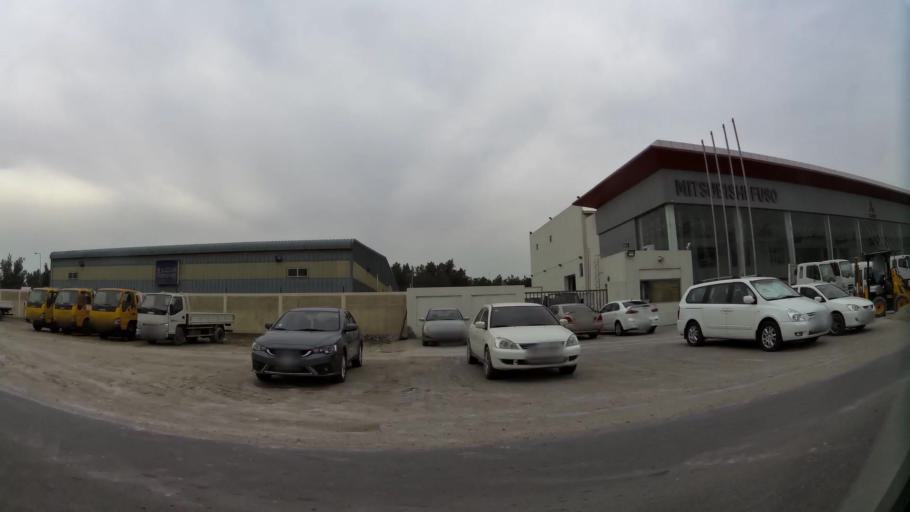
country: BH
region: Northern
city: Sitrah
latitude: 26.1284
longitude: 50.6020
